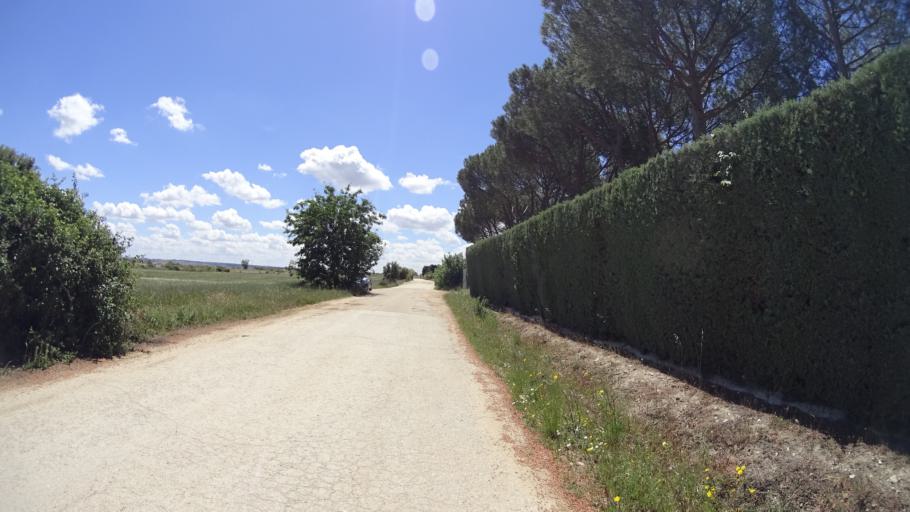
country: ES
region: Madrid
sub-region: Provincia de Madrid
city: Villanueva del Pardillo
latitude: 40.4868
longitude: -3.9867
